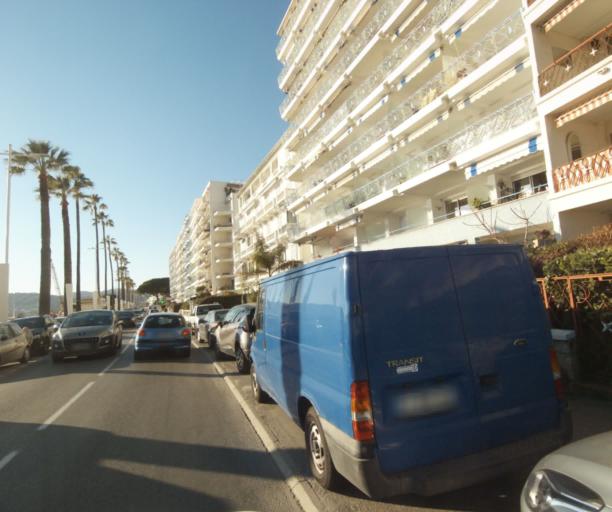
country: FR
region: Provence-Alpes-Cote d'Azur
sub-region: Departement des Alpes-Maritimes
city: Antibes
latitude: 43.5705
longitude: 7.1046
